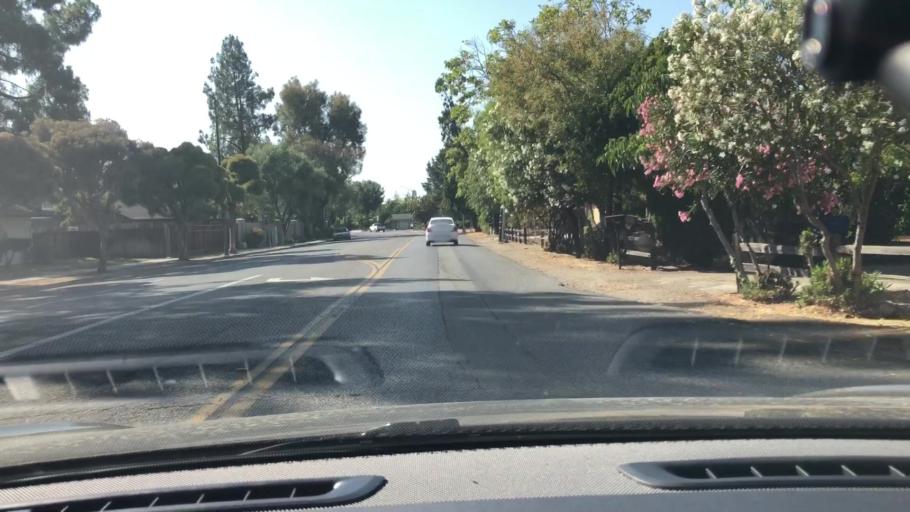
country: US
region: California
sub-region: Santa Clara County
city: Campbell
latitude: 37.2641
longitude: -121.9721
